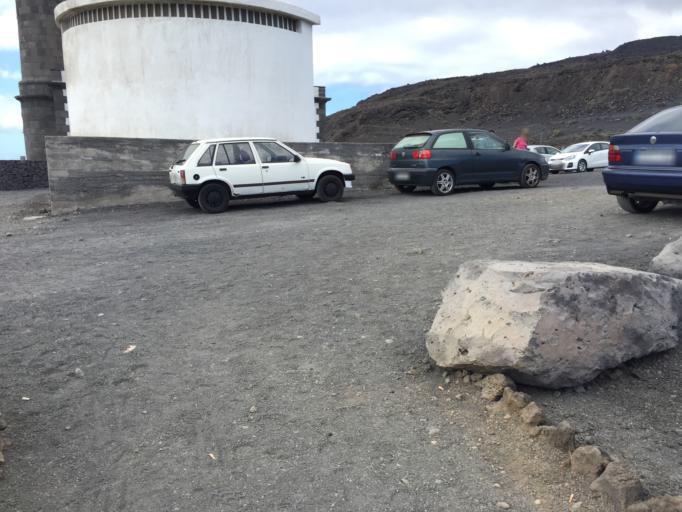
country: ES
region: Canary Islands
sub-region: Provincia de Santa Cruz de Tenerife
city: Fuencaliente de la Palma
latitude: 28.4553
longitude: -17.8430
